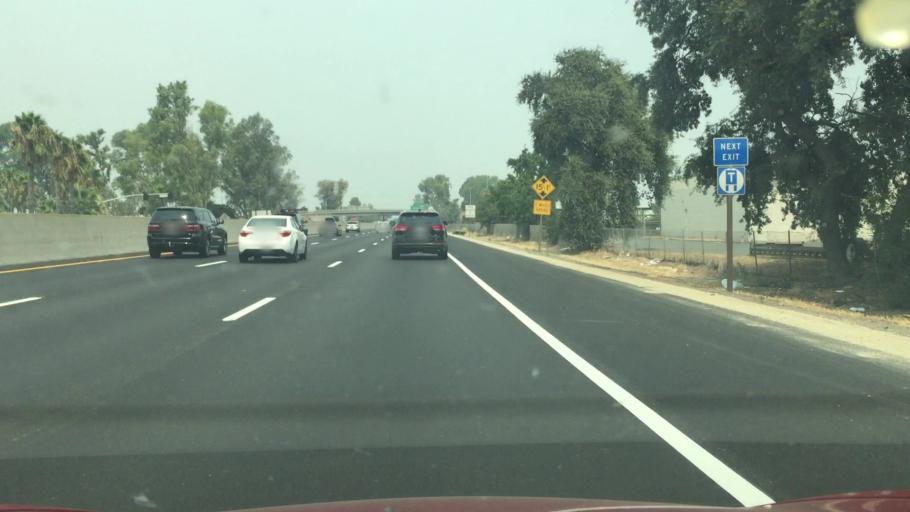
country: US
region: California
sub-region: San Joaquin County
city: August
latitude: 37.9891
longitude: -121.2514
